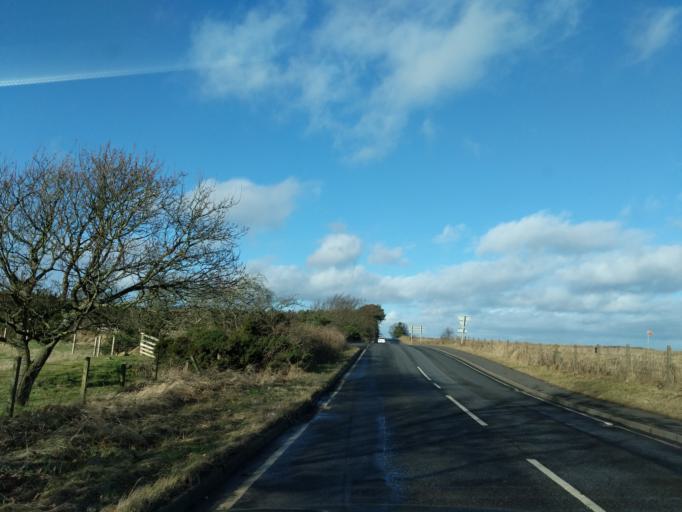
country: GB
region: Scotland
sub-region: West Lothian
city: Kirknewton
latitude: 55.8699
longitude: -3.4050
